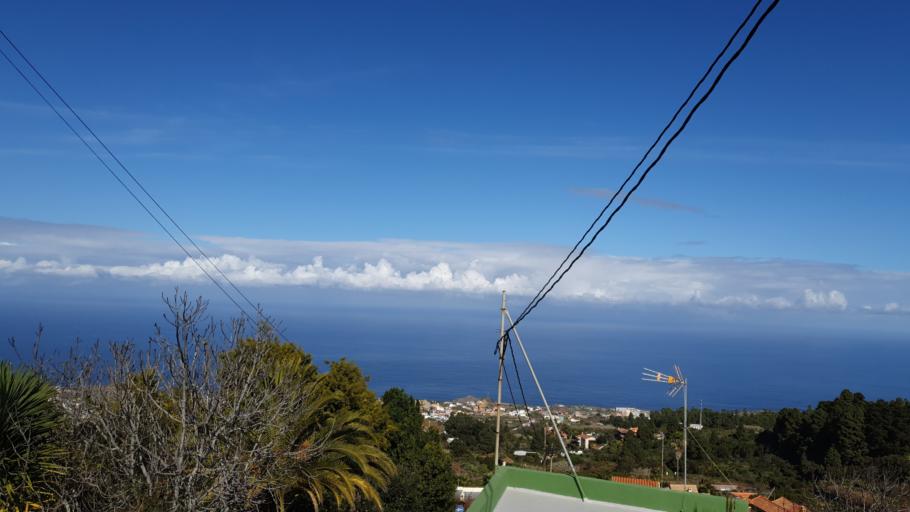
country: ES
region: Canary Islands
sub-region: Provincia de Santa Cruz de Tenerife
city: La Guancha
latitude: 28.3579
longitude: -16.6842
